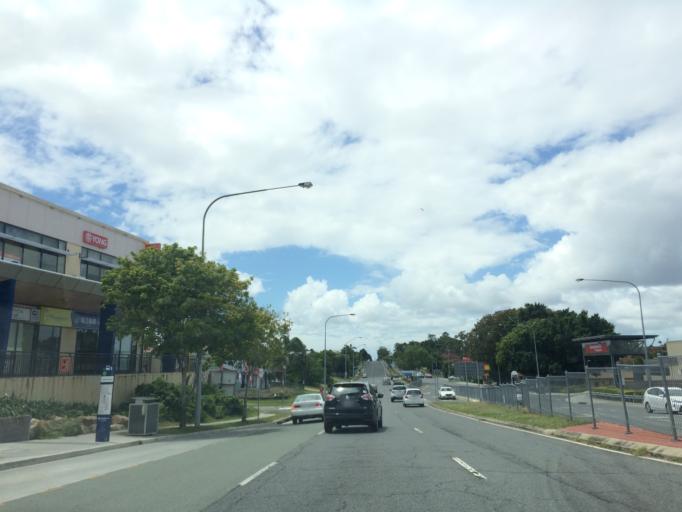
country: AU
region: Queensland
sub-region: Brisbane
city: Sunnybank Hills
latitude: -27.6108
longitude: 153.0543
